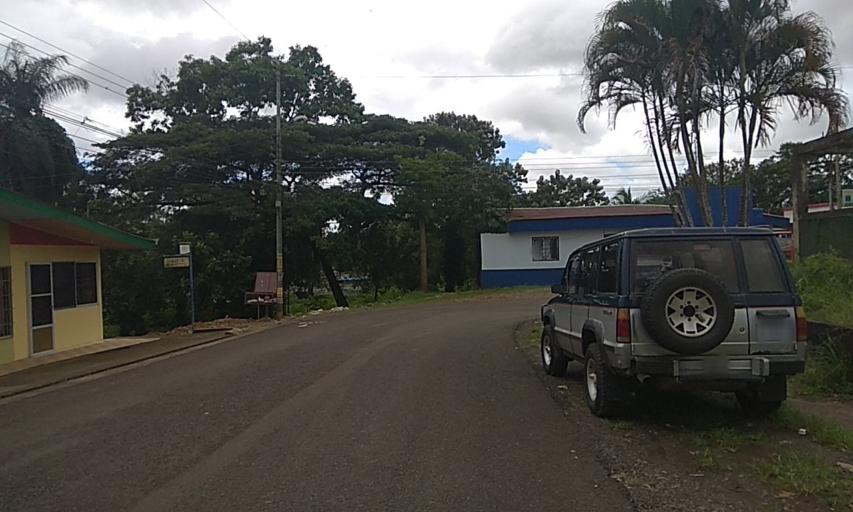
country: CR
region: Alajuela
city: Los Chiles
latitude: 11.0302
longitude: -84.7175
